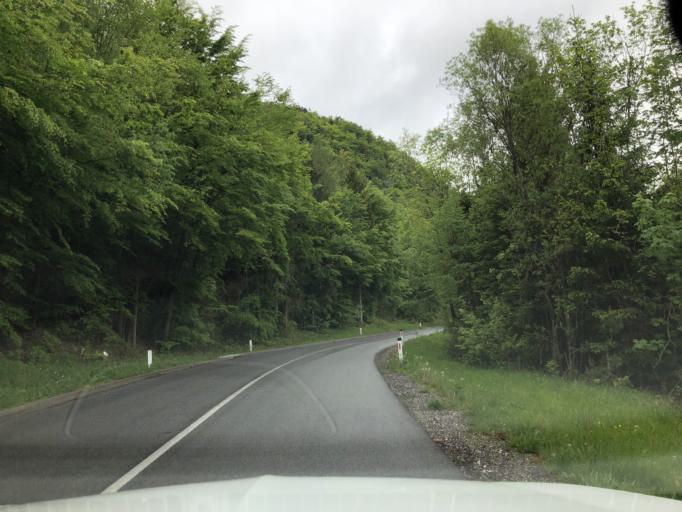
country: SI
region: Jesenice
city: Slovenski Javornik
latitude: 46.4139
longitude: 14.0904
